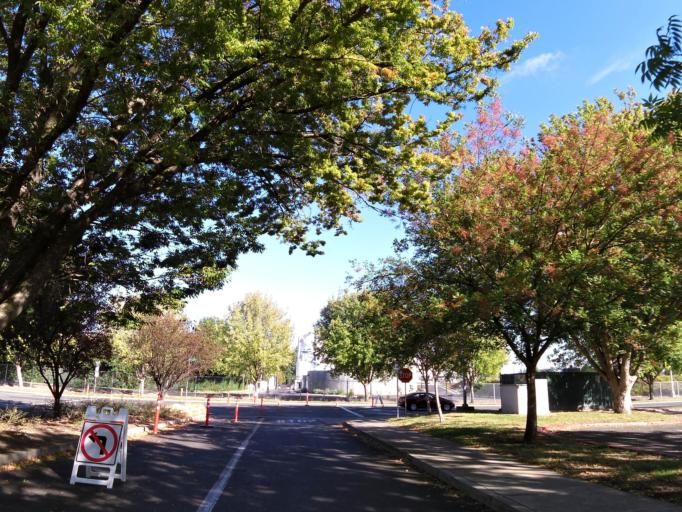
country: US
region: California
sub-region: Sacramento County
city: Rosemont
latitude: 38.5557
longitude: -121.4191
